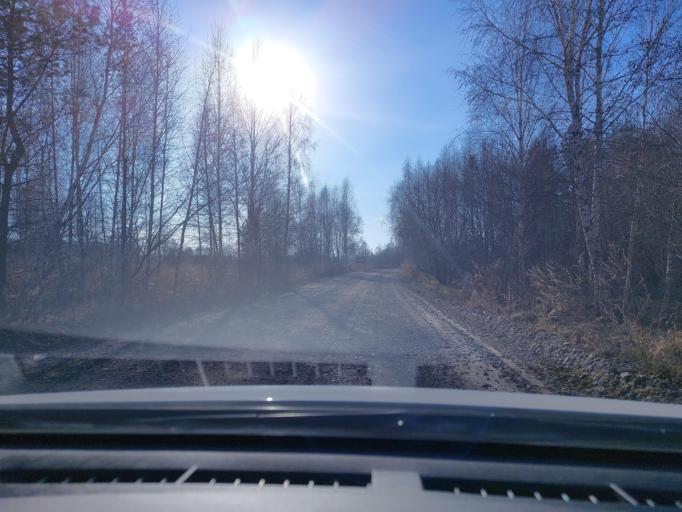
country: RU
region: Irkutsk
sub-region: Irkutskiy Rayon
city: Irkutsk
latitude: 52.3022
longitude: 104.2761
